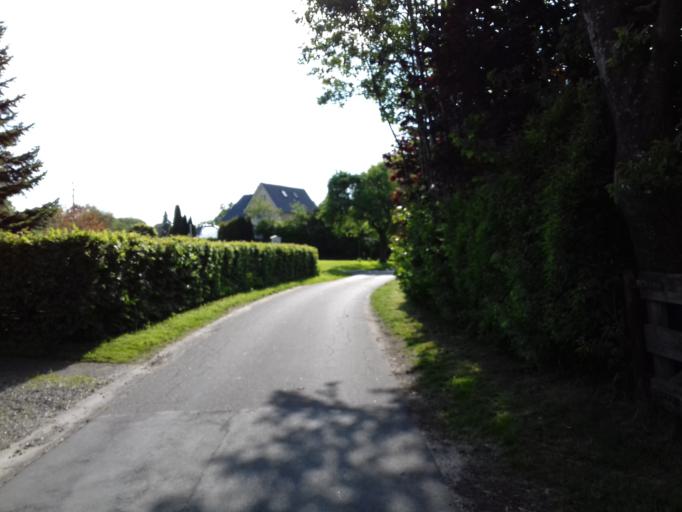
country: DE
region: Schleswig-Holstein
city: Tasdorf
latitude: 54.0792
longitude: 10.0196
